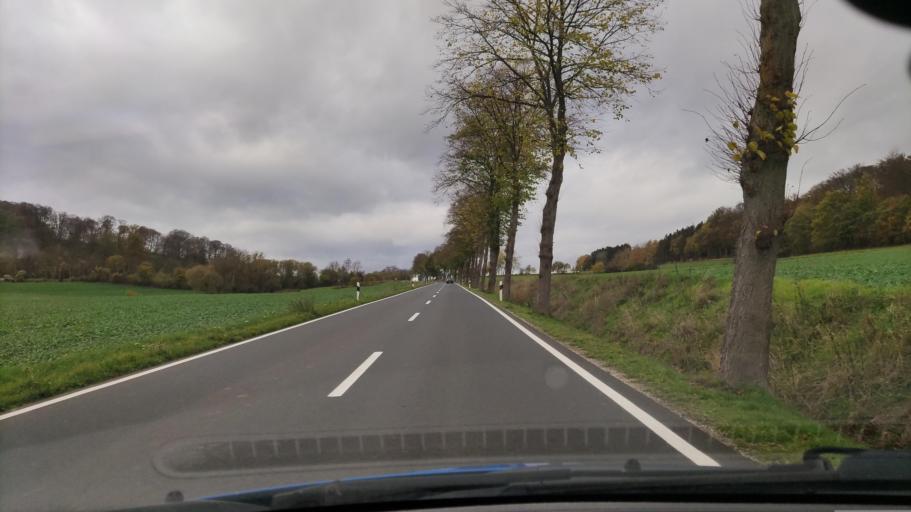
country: DE
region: Lower Saxony
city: Wangelnstedt
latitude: 51.8632
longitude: 9.7108
